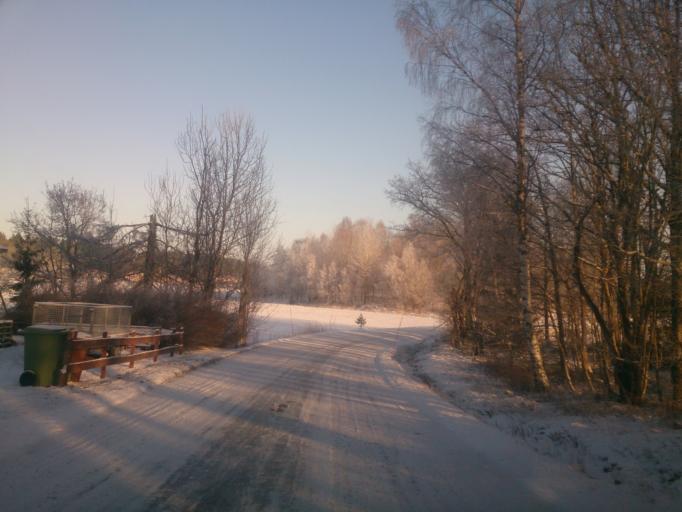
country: SE
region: OEstergoetland
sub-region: Norrkopings Kommun
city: Krokek
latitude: 58.4999
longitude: 16.5768
